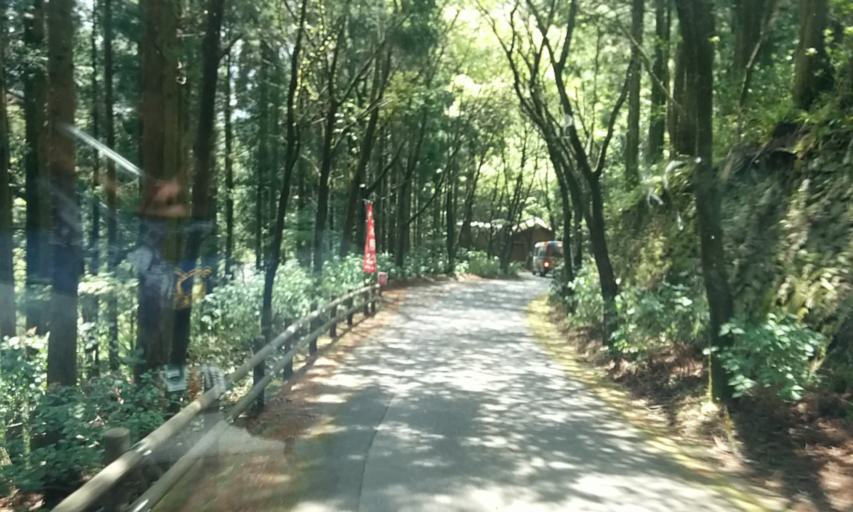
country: JP
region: Ehime
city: Niihama
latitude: 33.8776
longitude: 133.3120
